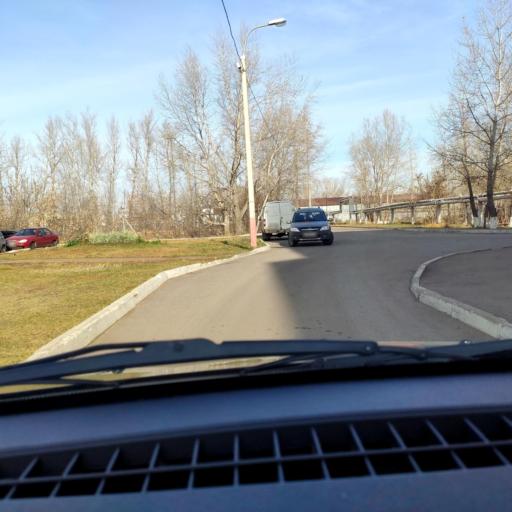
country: RU
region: Bashkortostan
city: Ufa
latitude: 54.6660
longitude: 55.9421
